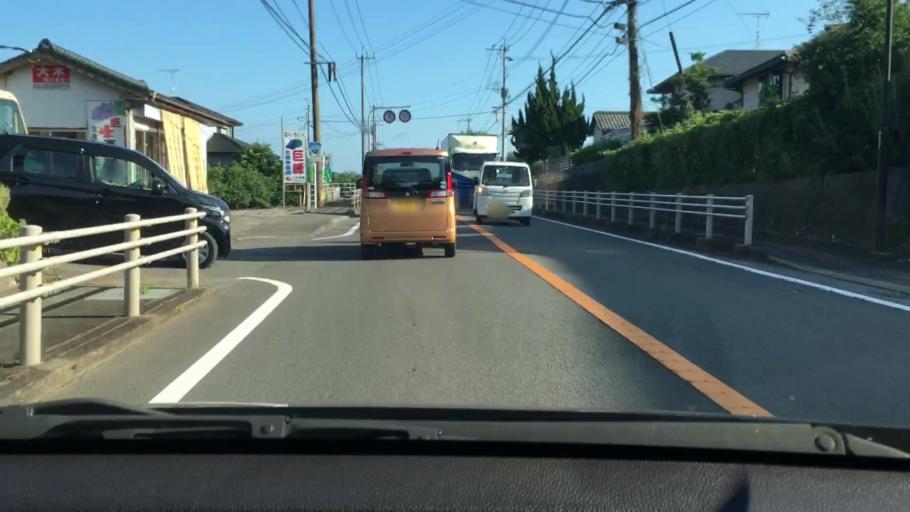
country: JP
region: Nagasaki
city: Togitsu
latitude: 32.9014
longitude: 129.7804
